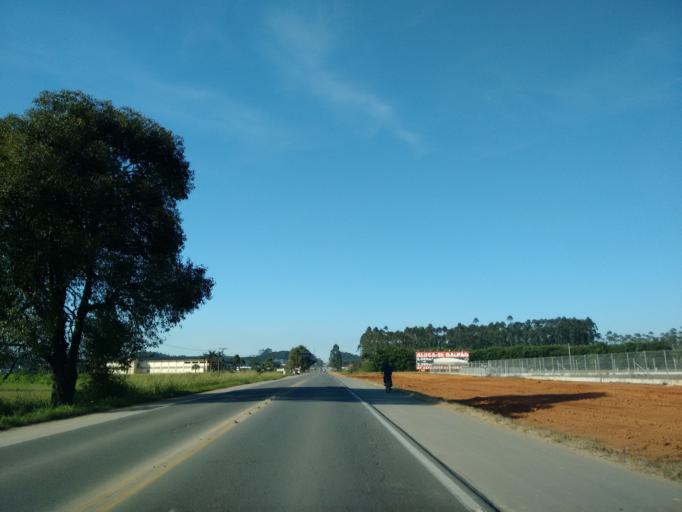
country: BR
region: Santa Catarina
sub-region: Guaramirim
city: Guaramirim
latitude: -26.4665
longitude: -48.9583
